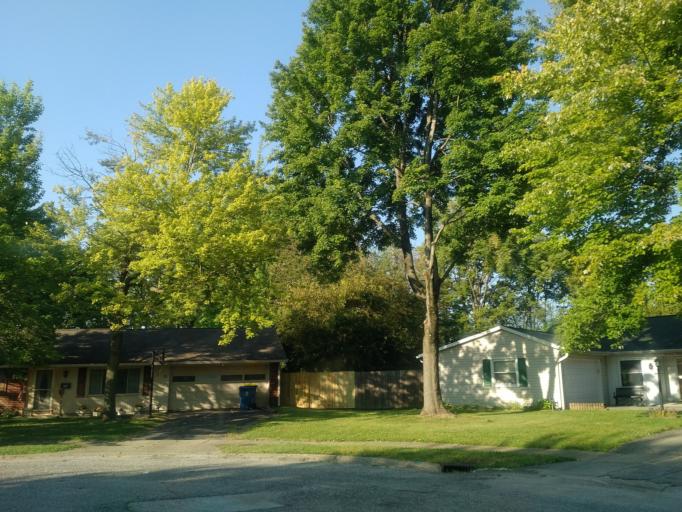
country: US
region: Indiana
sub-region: Marion County
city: Cumberland
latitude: 39.7922
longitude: -85.9886
